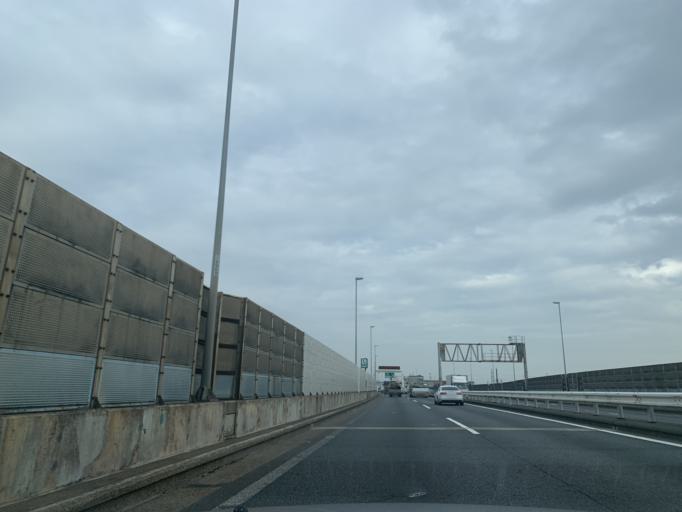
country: JP
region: Saitama
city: Yashio-shi
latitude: 35.8089
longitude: 139.8391
